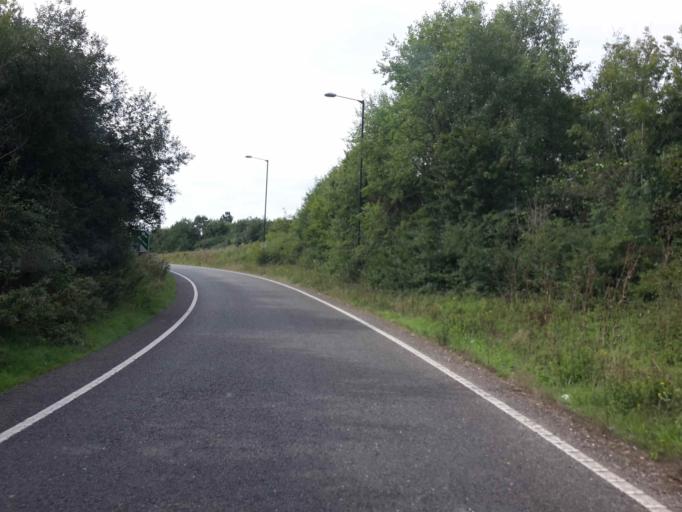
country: GB
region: England
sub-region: West Sussex
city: Ashington
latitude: 50.9365
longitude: -0.3859
